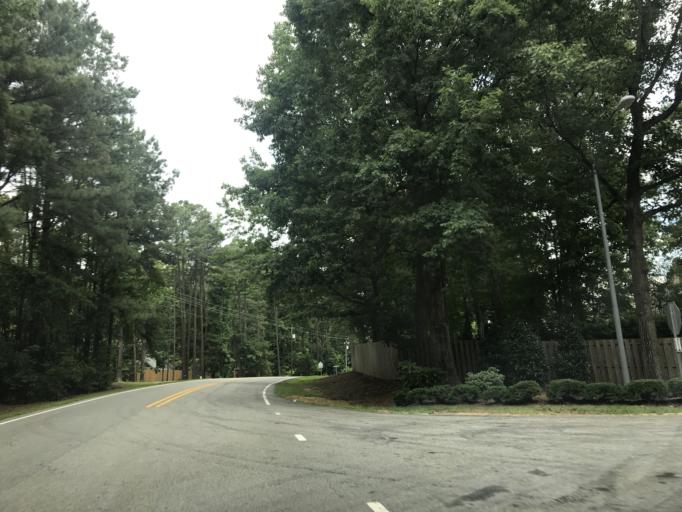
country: US
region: North Carolina
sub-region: Wake County
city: West Raleigh
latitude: 35.9123
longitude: -78.6943
